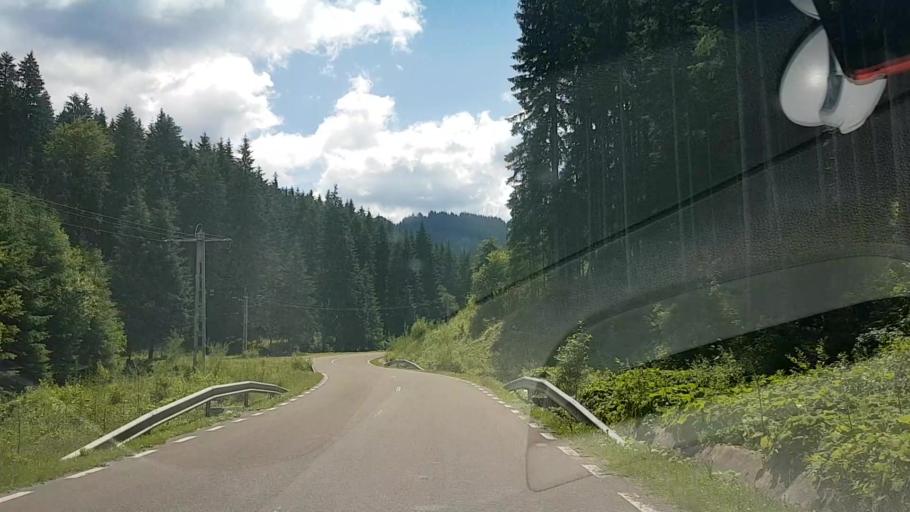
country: RO
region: Suceava
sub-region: Comuna Sadova
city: Sadova
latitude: 47.4750
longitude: 25.5011
